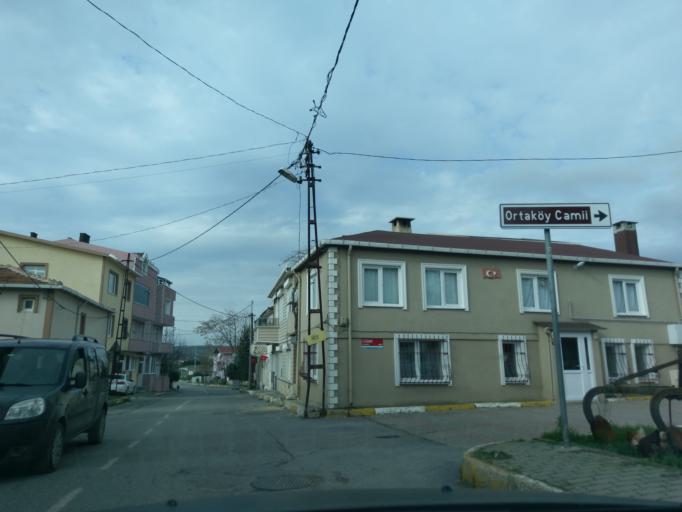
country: TR
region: Istanbul
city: Ortakoy
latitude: 41.1009
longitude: 28.3746
